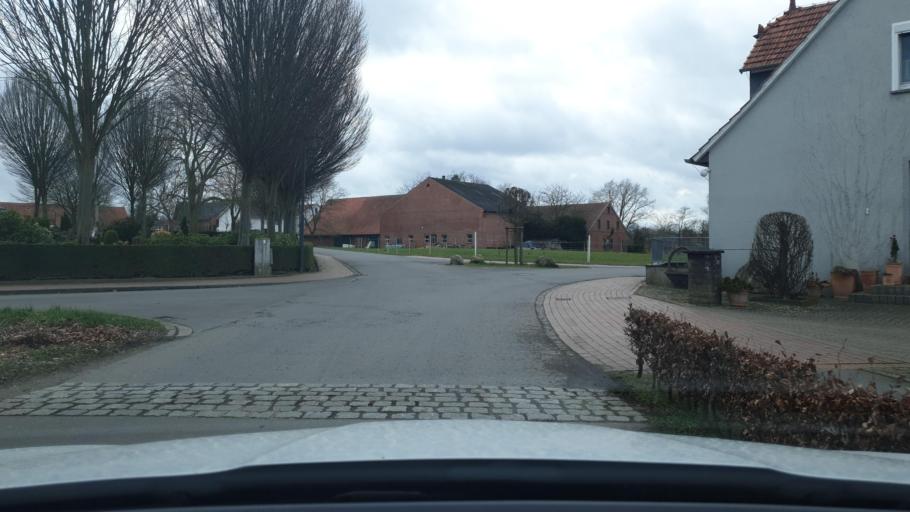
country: DE
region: North Rhine-Westphalia
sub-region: Regierungsbezirk Detmold
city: Hille
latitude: 52.3359
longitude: 8.7497
